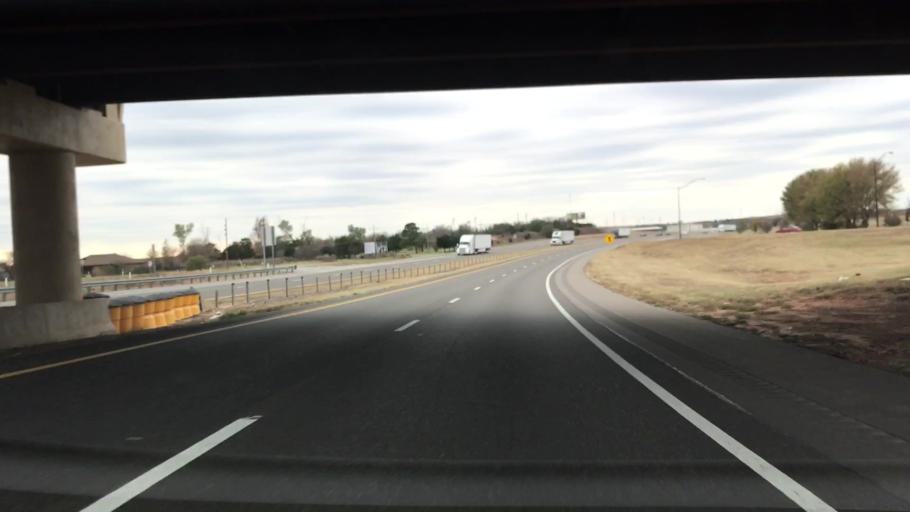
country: US
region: Oklahoma
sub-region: Custer County
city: Weatherford
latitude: 35.5238
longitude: -98.6932
